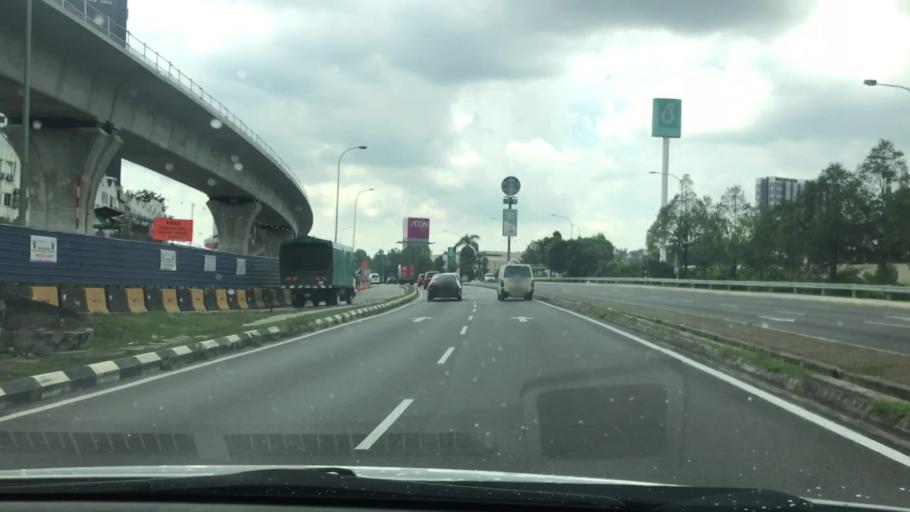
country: MY
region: Putrajaya
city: Putrajaya
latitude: 2.9952
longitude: 101.6779
